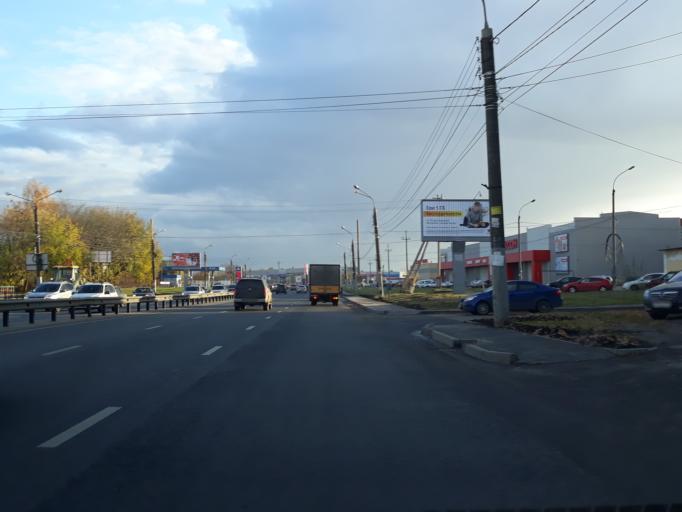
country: RU
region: Nizjnij Novgorod
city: Nizhniy Novgorod
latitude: 56.3135
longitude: 43.8991
